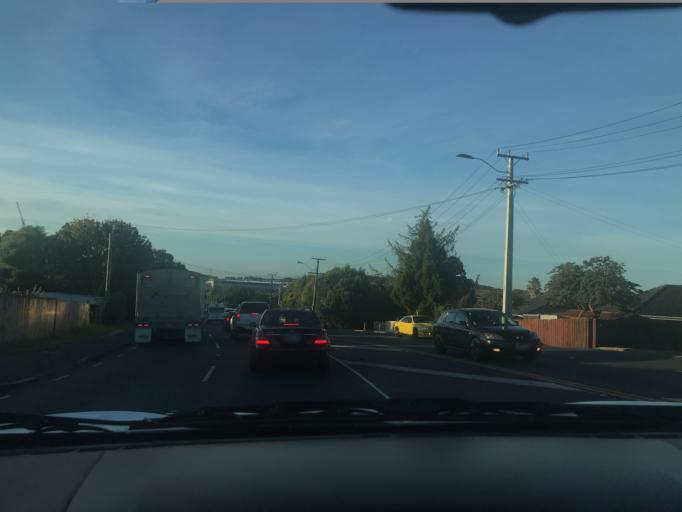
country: NZ
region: Auckland
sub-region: Auckland
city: Tamaki
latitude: -36.9104
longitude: 174.8377
